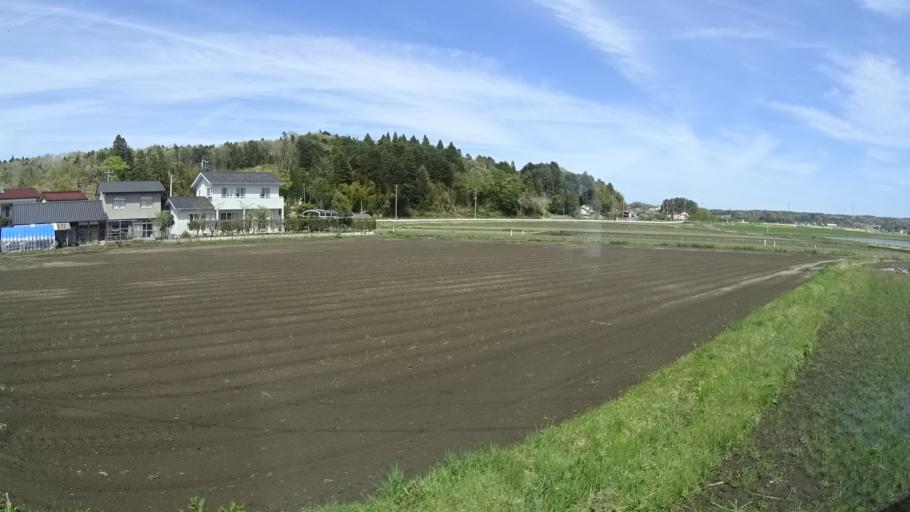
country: JP
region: Fukushima
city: Namie
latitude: 37.6094
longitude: 140.9865
